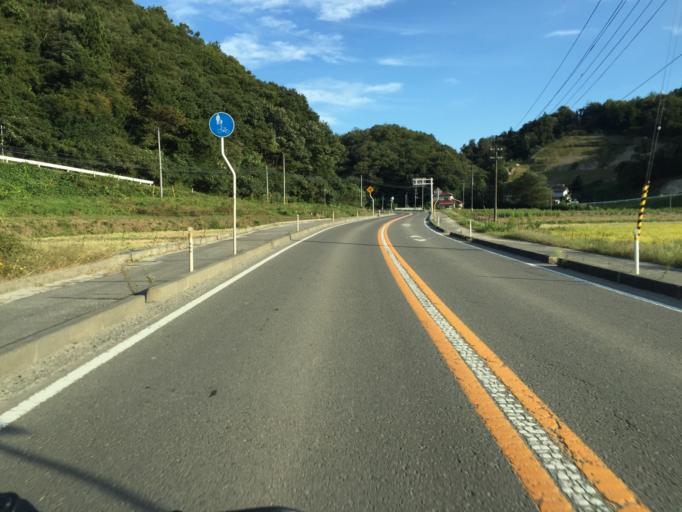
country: JP
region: Fukushima
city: Hobaramachi
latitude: 37.6915
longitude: 140.6102
